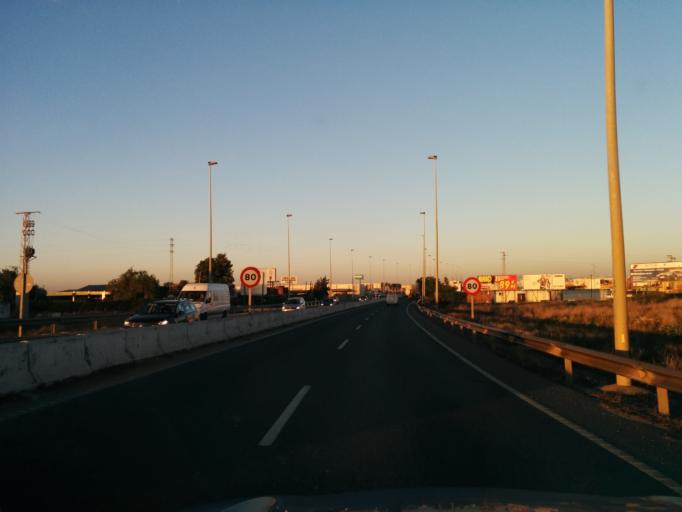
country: ES
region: Andalusia
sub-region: Provincia de Sevilla
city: Sevilla
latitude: 37.3690
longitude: -5.9356
